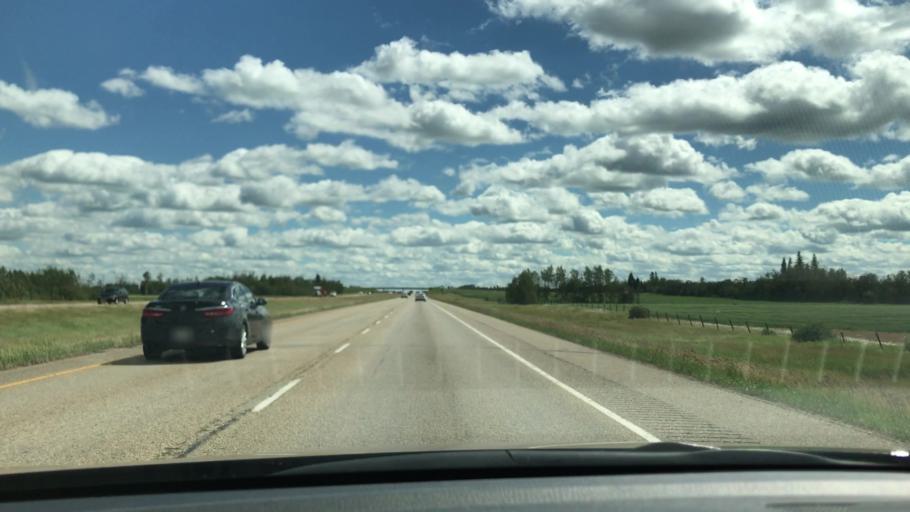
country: CA
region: Alberta
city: Leduc
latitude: 53.1437
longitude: -113.5984
